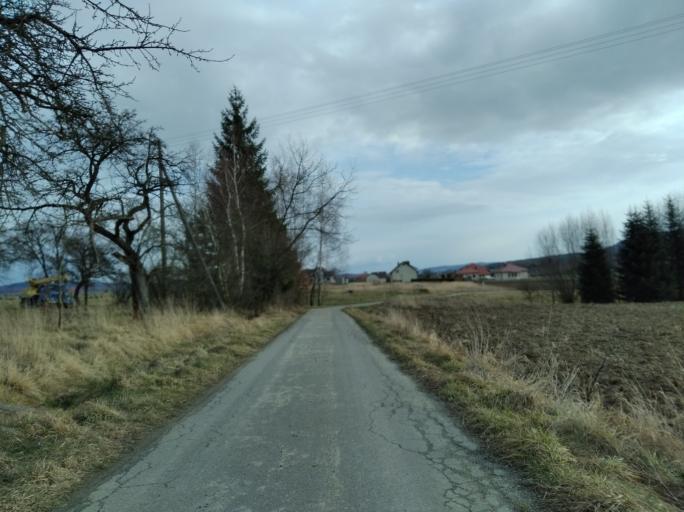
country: PL
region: Subcarpathian Voivodeship
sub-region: Powiat strzyzowski
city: Strzyzow
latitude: 49.8519
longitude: 21.7733
